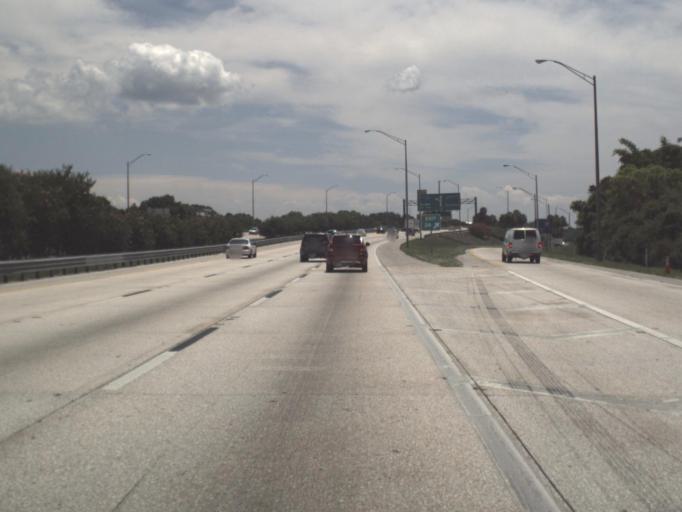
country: US
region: Florida
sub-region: Pinellas County
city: Saint Petersburg
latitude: 27.7955
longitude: -82.6616
